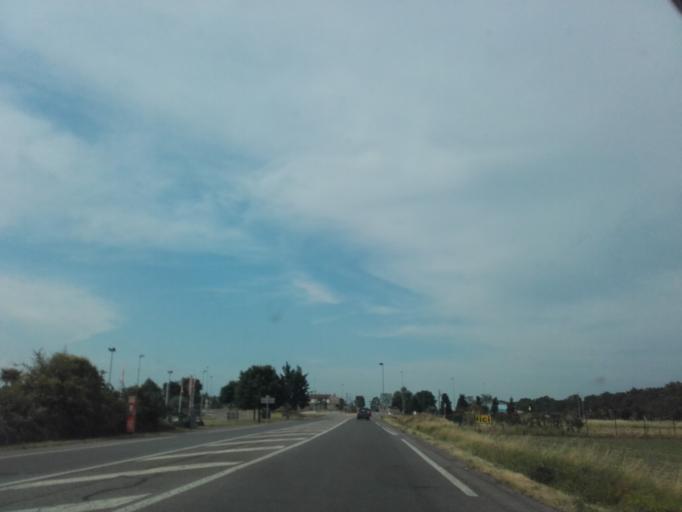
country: FR
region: Rhone-Alpes
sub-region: Departement de la Drome
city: Livron-sur-Drome
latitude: 44.8066
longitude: 4.8558
